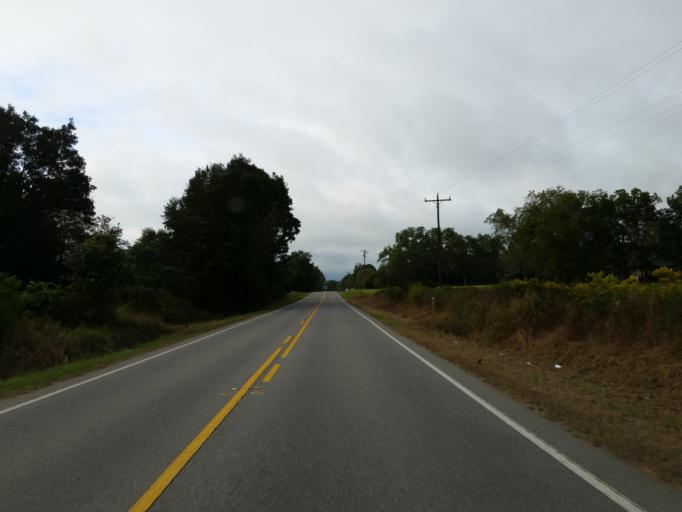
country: US
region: Georgia
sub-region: Tift County
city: Tifton
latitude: 31.5805
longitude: -83.5718
